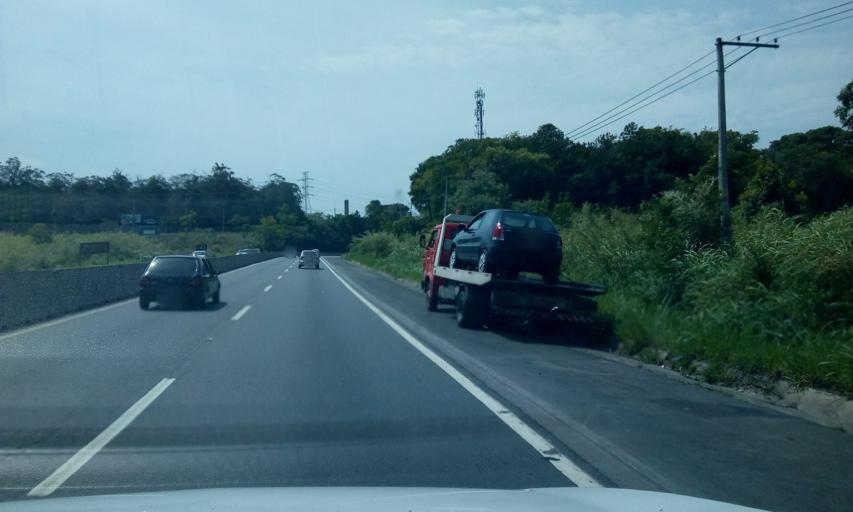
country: BR
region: Sao Paulo
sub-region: Itupeva
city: Itupeva
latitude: -23.1794
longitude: -46.9739
